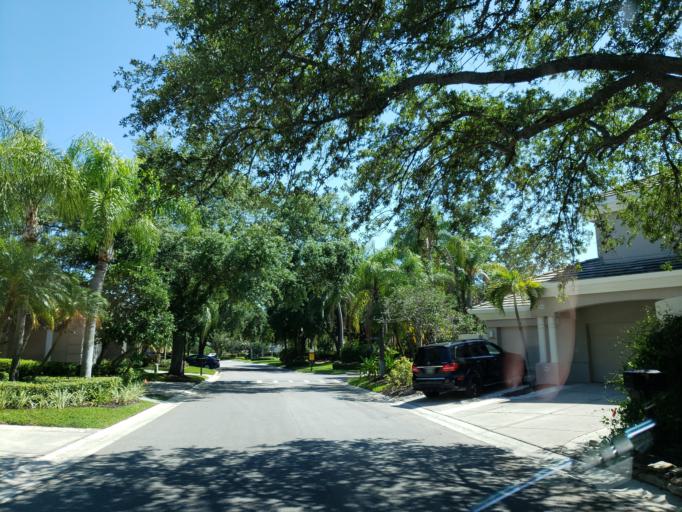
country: US
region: Florida
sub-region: Hillsborough County
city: Tampa
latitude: 27.9352
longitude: -82.4524
